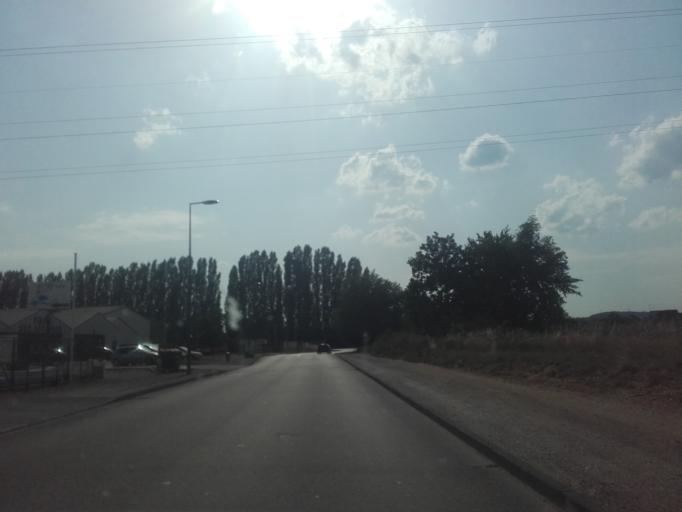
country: FR
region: Bourgogne
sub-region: Departement de la Cote-d'Or
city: Beaune
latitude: 47.0238
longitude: 4.8603
